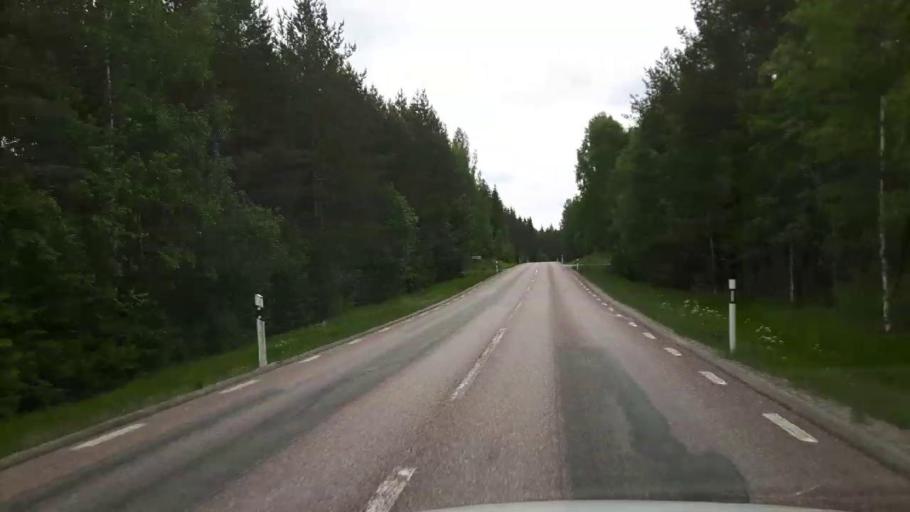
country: SE
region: Dalarna
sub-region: Hedemora Kommun
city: Brunna
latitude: 60.1781
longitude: 15.9985
